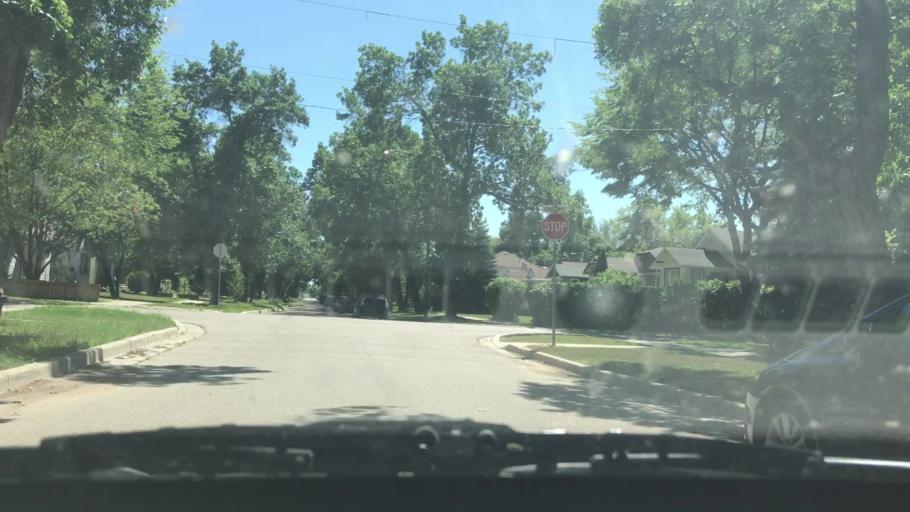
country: CA
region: Manitoba
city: Winnipeg
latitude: 49.8711
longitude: -97.1959
